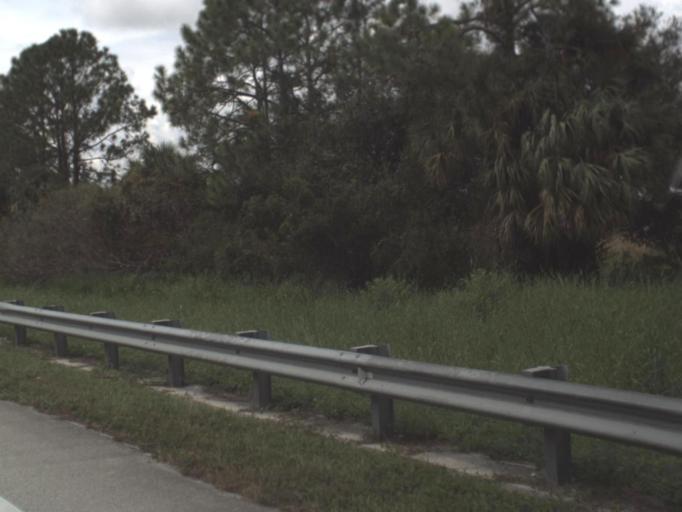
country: US
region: Florida
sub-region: Hendry County
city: Port LaBelle
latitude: 26.8405
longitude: -81.3887
